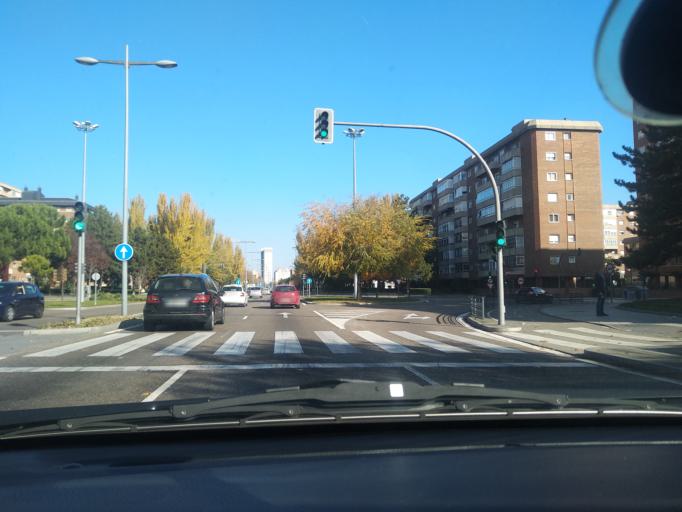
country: ES
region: Castille and Leon
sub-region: Provincia de Valladolid
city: Valladolid
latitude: 41.6503
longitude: -4.7395
